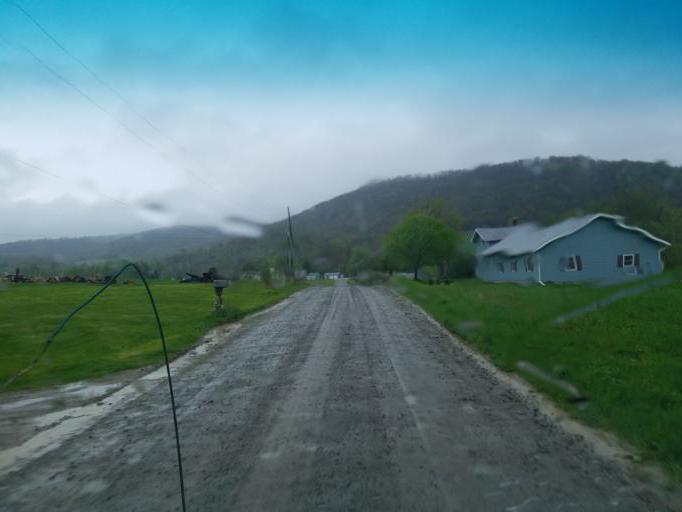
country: US
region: Pennsylvania
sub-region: Tioga County
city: Westfield
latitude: 41.9173
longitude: -77.6254
